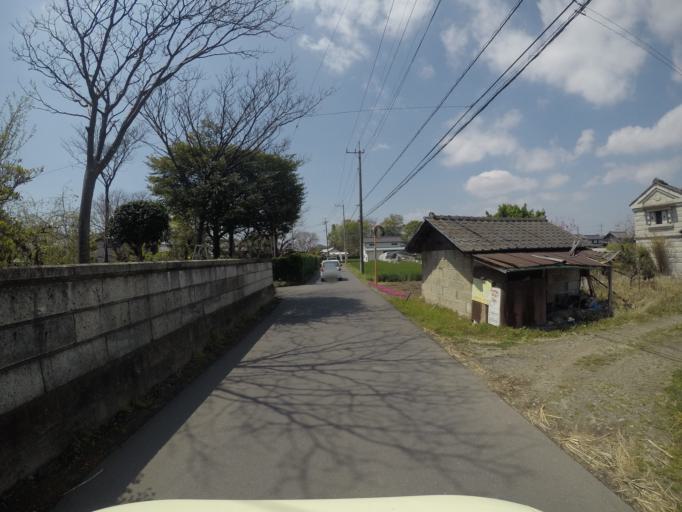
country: JP
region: Tochigi
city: Mibu
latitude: 36.4405
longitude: 139.7846
